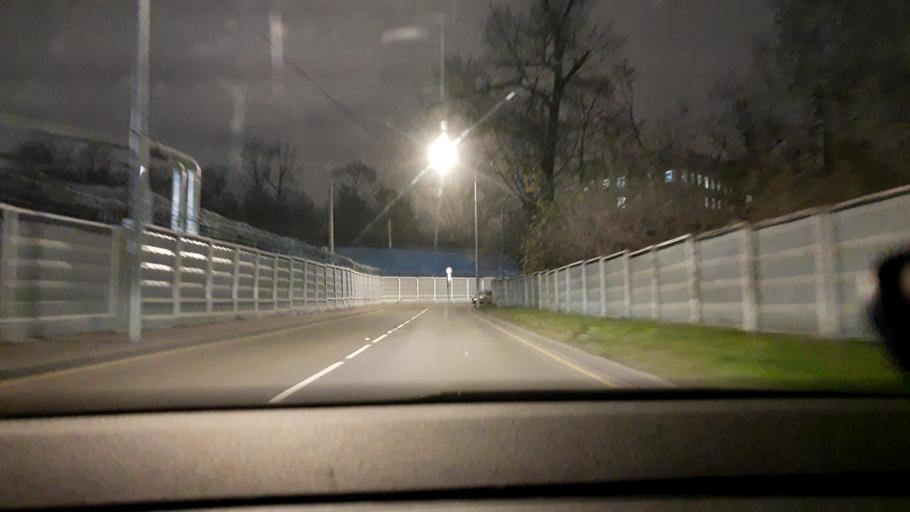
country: RU
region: Moscow
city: Sokol'niki
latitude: 55.7987
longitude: 37.6446
